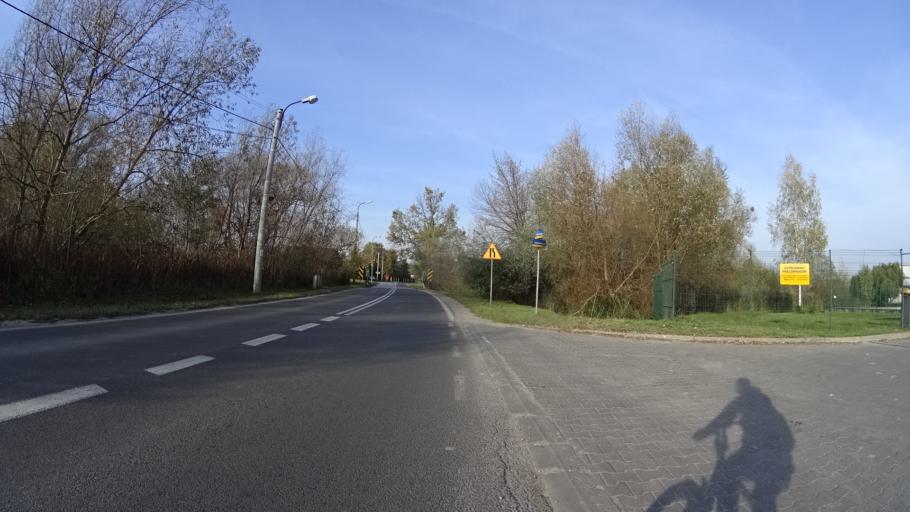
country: PL
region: Masovian Voivodeship
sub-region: Powiat warszawski zachodni
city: Babice
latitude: 52.2846
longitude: 20.8674
